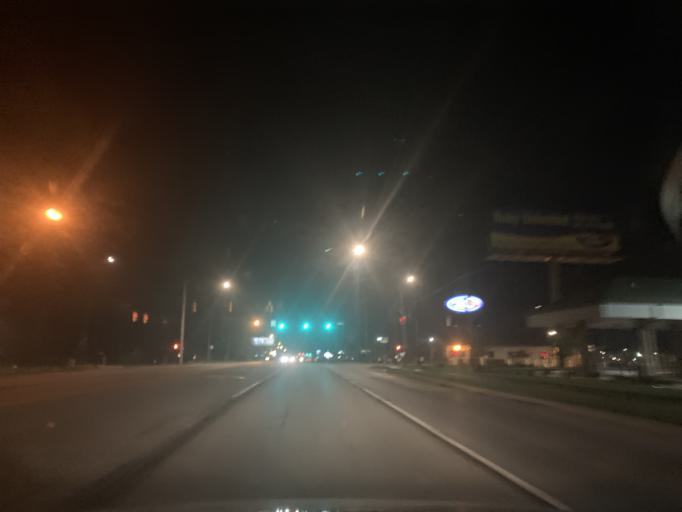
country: US
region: Indiana
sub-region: Saint Joseph County
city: Gulivoire Park
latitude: 41.6339
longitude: -86.2506
